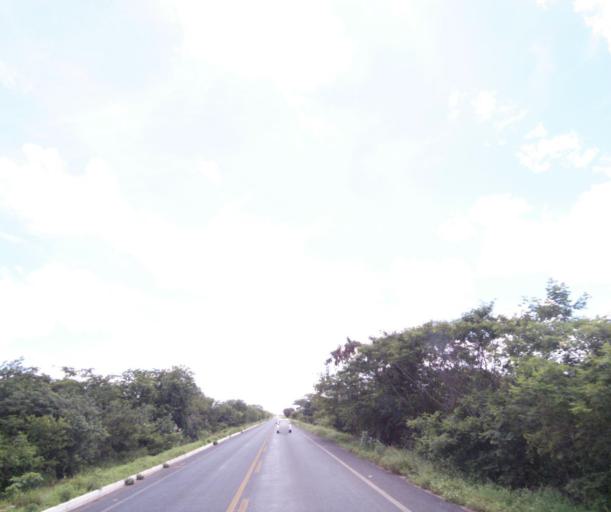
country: BR
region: Bahia
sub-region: Bom Jesus Da Lapa
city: Bom Jesus da Lapa
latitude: -13.2601
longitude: -43.5016
